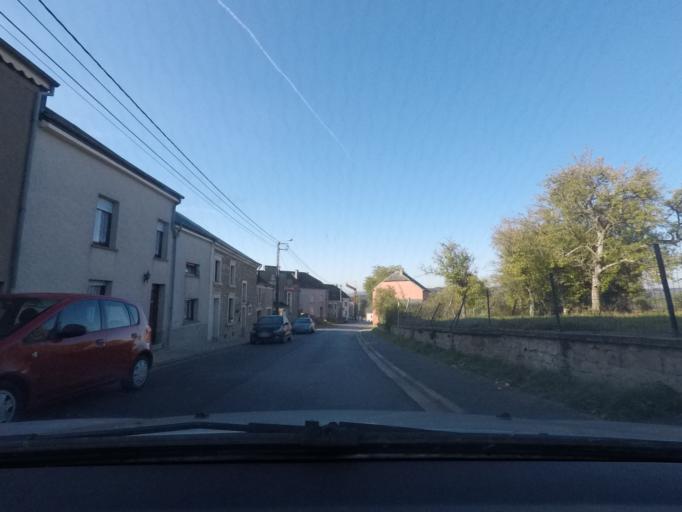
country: BE
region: Wallonia
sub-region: Province du Luxembourg
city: Messancy
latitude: 49.6301
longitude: 5.8016
